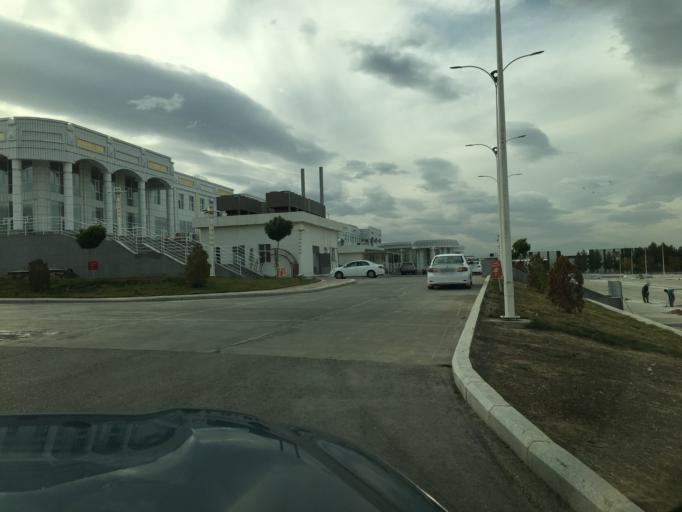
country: TM
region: Ahal
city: Ashgabat
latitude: 37.9022
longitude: 58.4151
